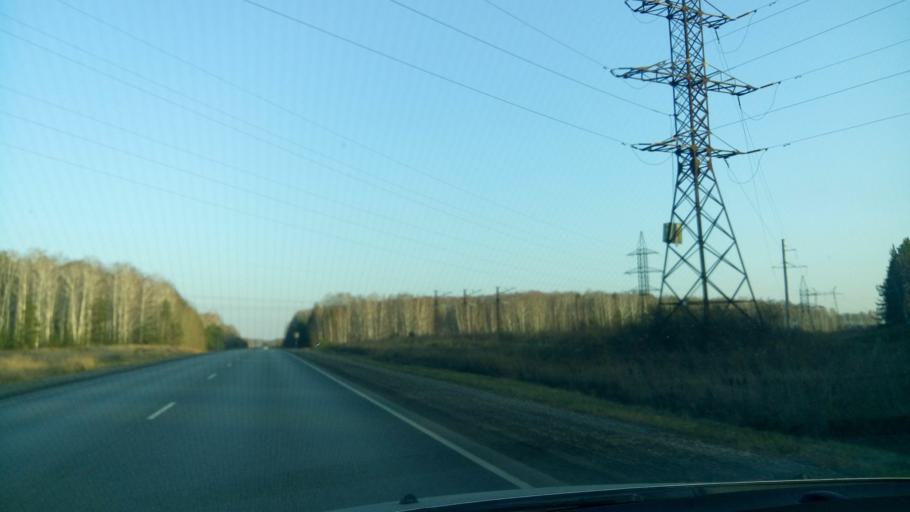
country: RU
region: Sverdlovsk
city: Baraba
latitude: 56.7791
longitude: 61.7997
